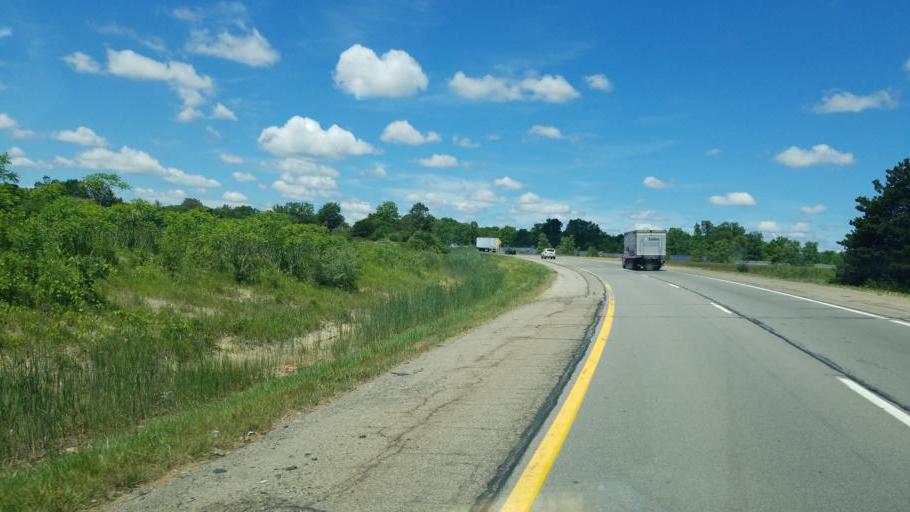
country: US
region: Michigan
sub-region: Washtenaw County
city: Ann Arbor
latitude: 42.3231
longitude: -83.6912
